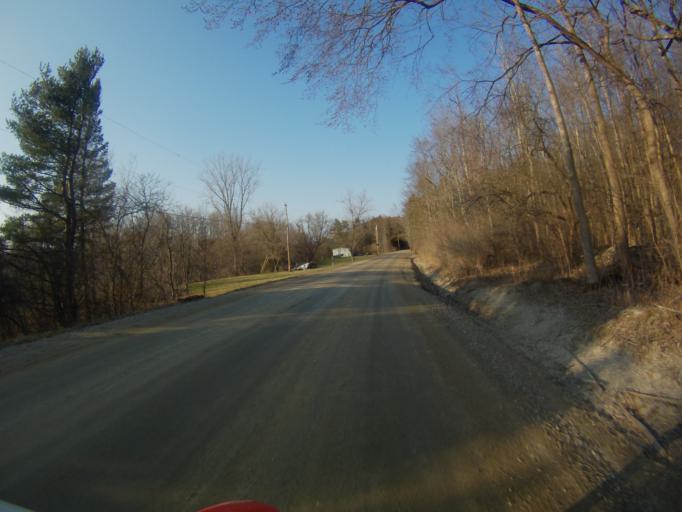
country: US
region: Vermont
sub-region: Addison County
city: Bristol
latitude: 44.1156
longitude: -73.0880
